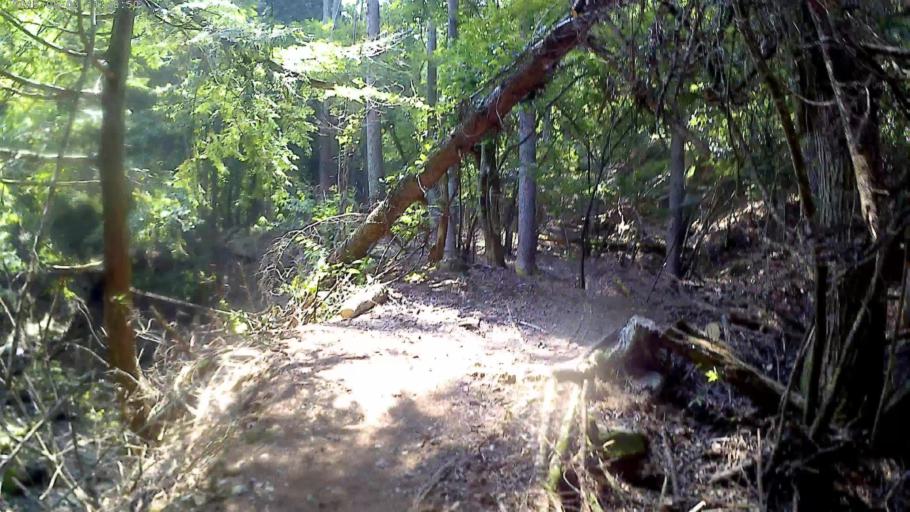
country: JP
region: Yamanashi
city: Enzan
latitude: 35.6160
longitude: 138.7754
